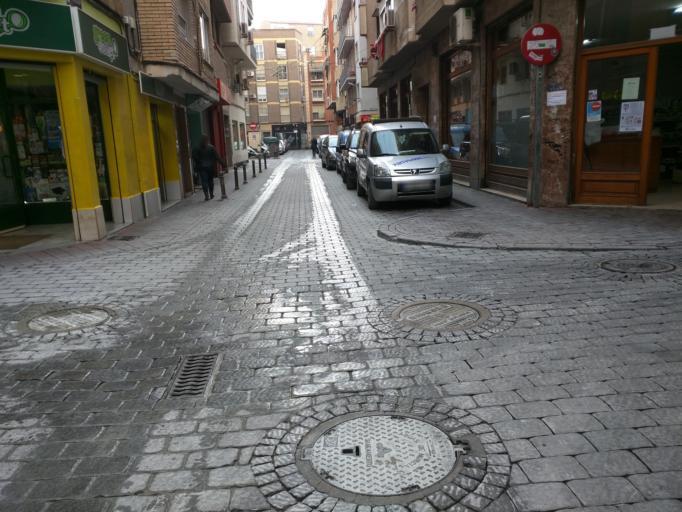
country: ES
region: Murcia
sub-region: Murcia
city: Murcia
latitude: 37.9868
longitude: -1.1255
